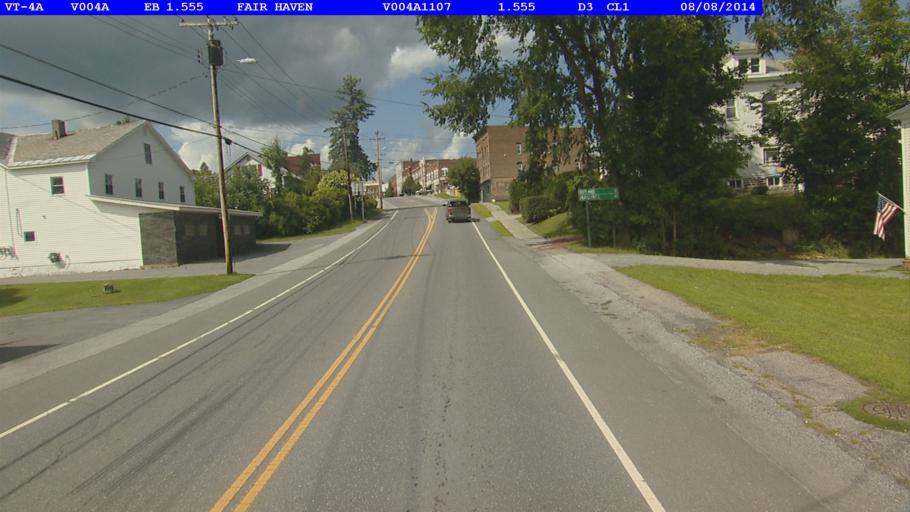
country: US
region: Vermont
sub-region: Rutland County
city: Fair Haven
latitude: 43.5906
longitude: -73.2650
